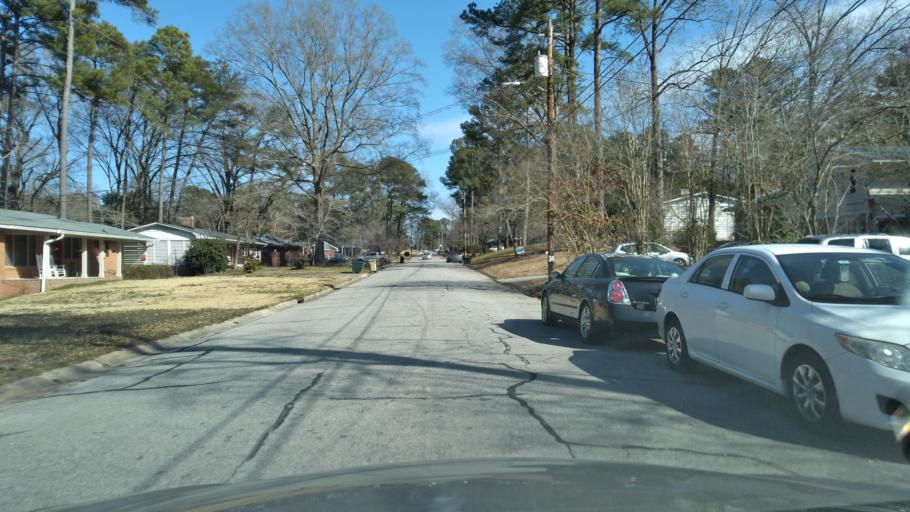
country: US
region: North Carolina
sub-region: Wake County
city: Garner
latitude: 35.6971
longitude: -78.6260
